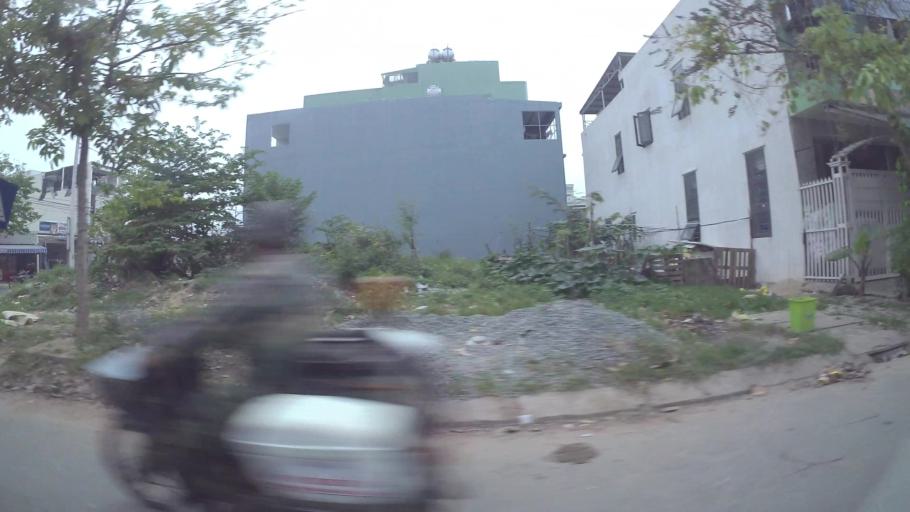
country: VN
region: Da Nang
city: Thanh Khe
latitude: 16.0442
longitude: 108.1790
